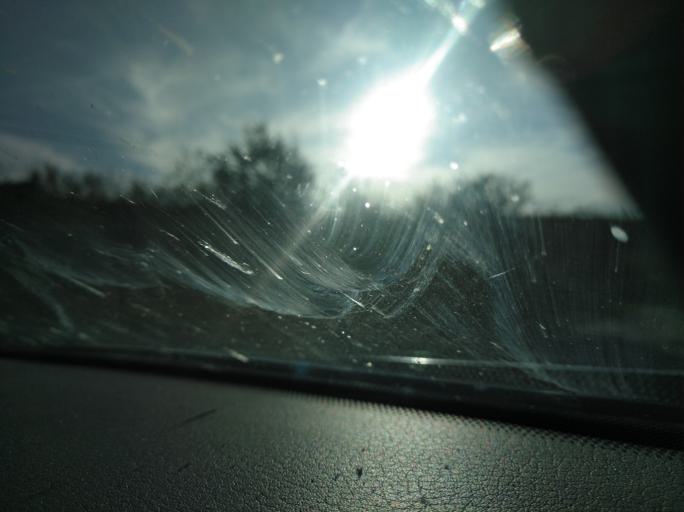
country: PT
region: Evora
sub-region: Borba
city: Borba
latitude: 38.9386
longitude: -7.4589
